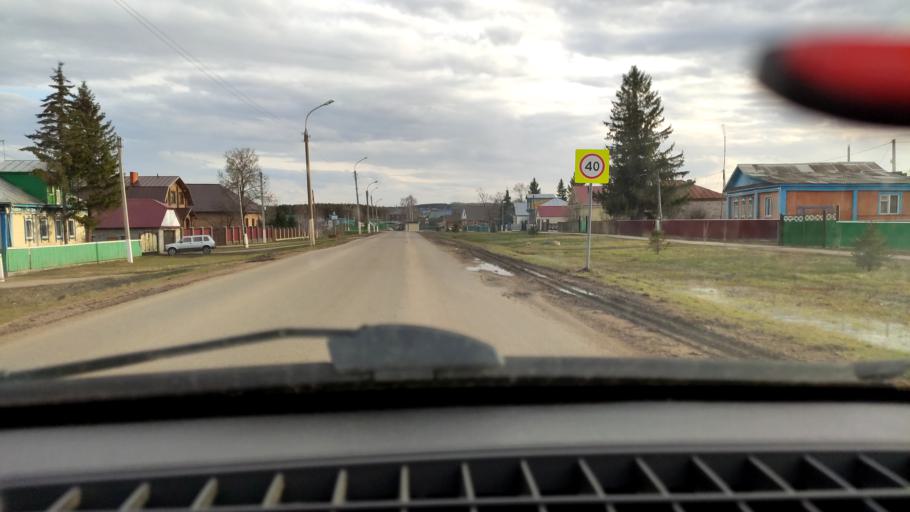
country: RU
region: Bashkortostan
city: Tolbazy
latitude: 54.0317
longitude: 55.8841
